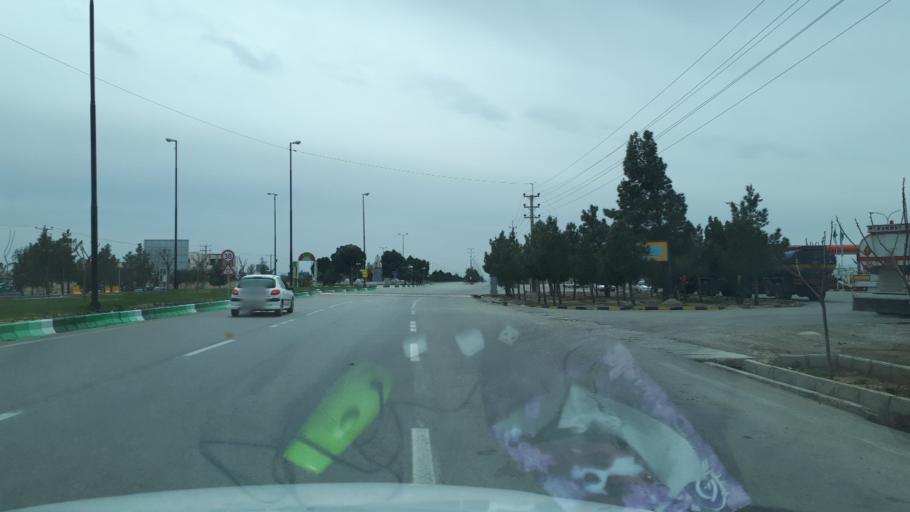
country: IR
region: Semnan
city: Damghan
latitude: 36.1526
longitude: 54.3283
